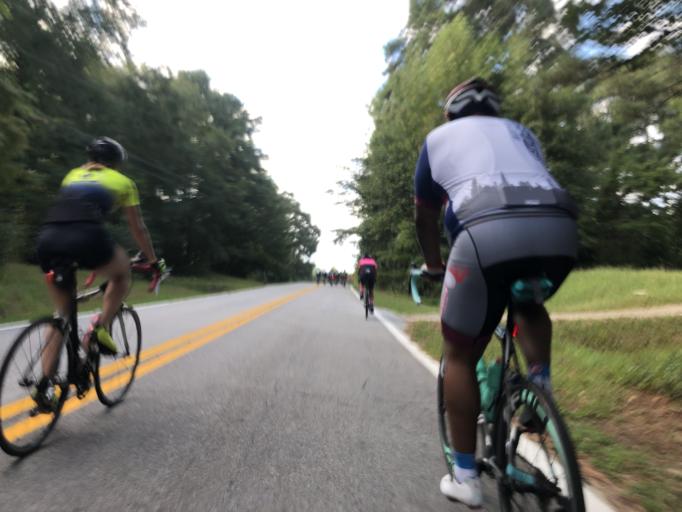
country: US
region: Georgia
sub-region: Fulton County
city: Palmetto
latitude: 33.5887
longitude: -84.6522
